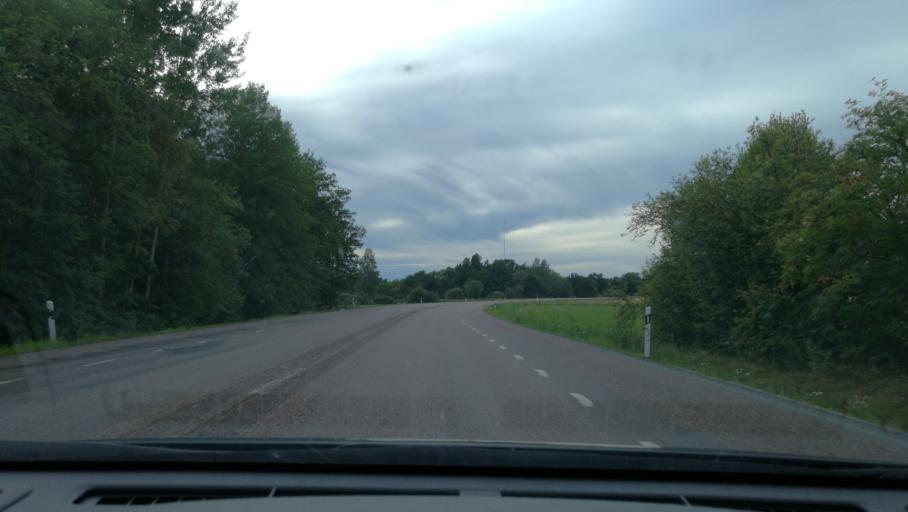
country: SE
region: Vaestmanland
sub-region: Kungsors Kommun
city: Kungsoer
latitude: 59.4372
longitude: 16.0557
